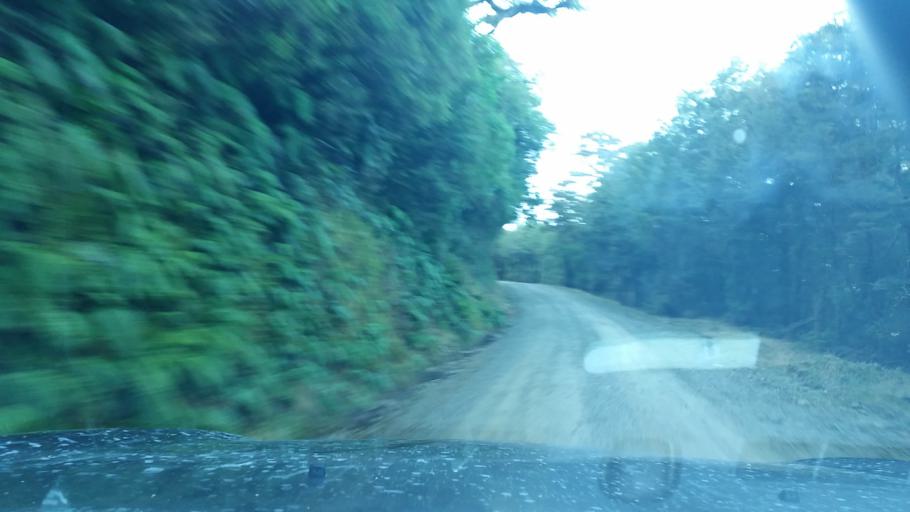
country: NZ
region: Marlborough
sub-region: Marlborough District
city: Picton
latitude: -41.0648
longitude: 174.1607
